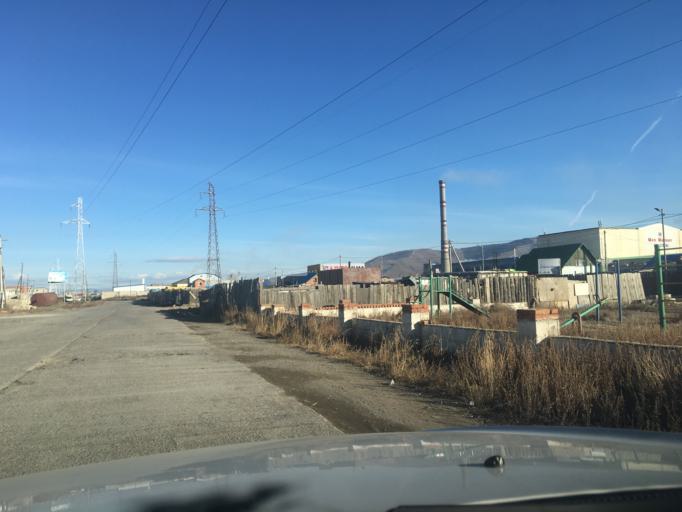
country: MN
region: Ulaanbaatar
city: Ulaanbaatar
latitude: 47.9011
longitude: 106.7880
